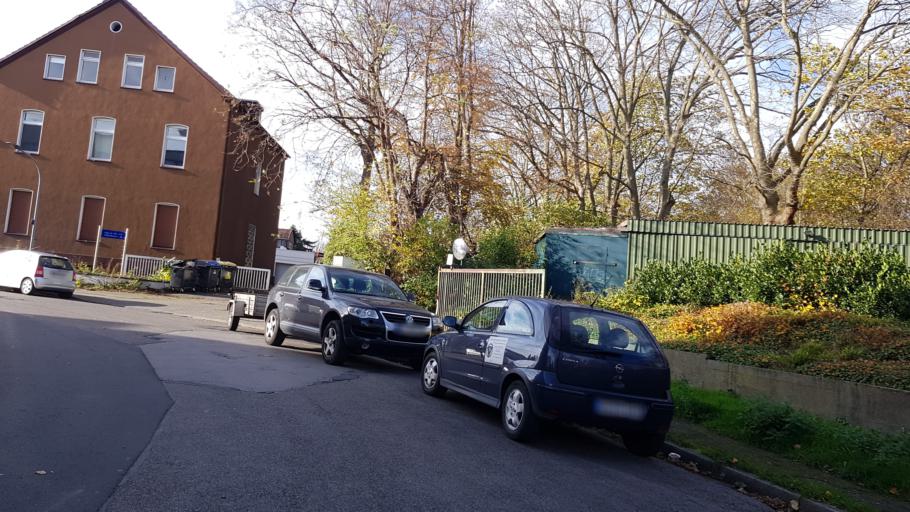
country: DE
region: North Rhine-Westphalia
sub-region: Regierungsbezirk Munster
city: Gelsenkirchen
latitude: 51.4911
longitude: 7.1381
